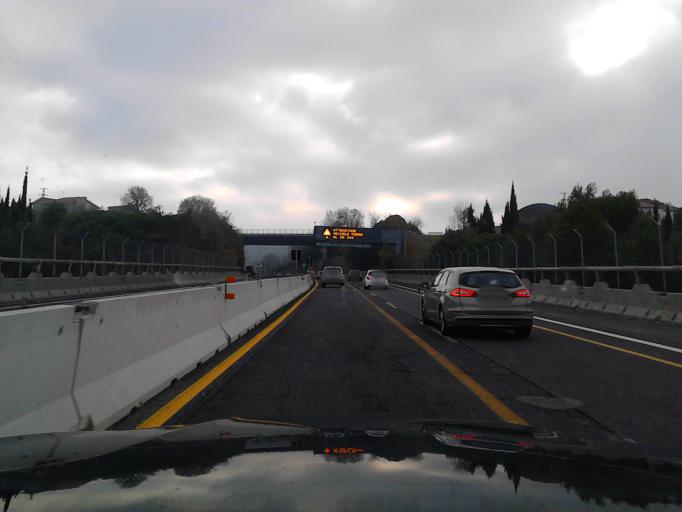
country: IT
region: Abruzzo
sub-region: Provincia di Teramo
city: Salino
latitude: 42.7726
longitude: 13.9304
